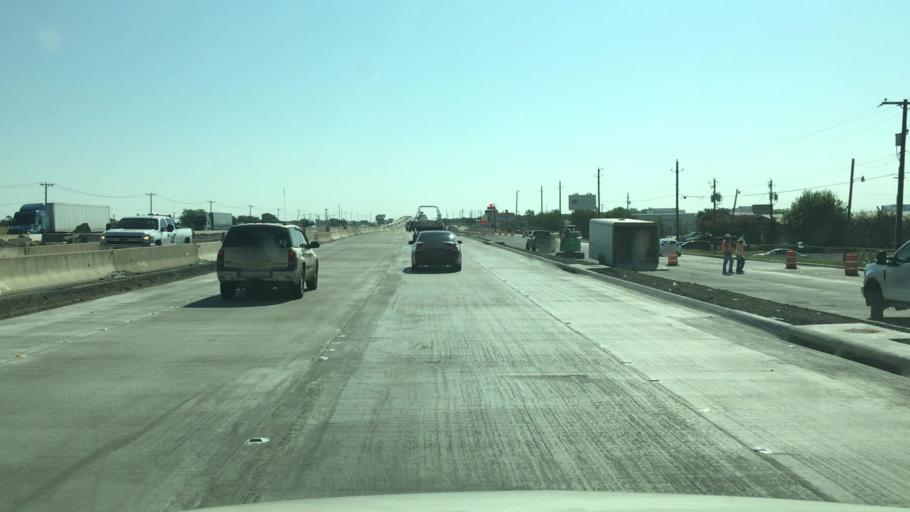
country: US
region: Texas
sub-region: Rockwall County
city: Rockwall
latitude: 32.9175
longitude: -96.4263
